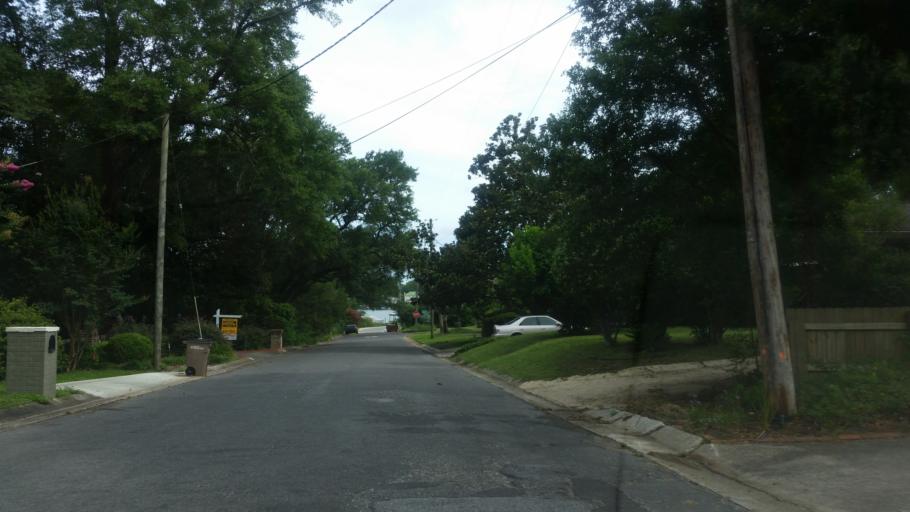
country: US
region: Florida
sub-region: Escambia County
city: East Pensacola Heights
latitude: 30.4435
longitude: -87.1904
